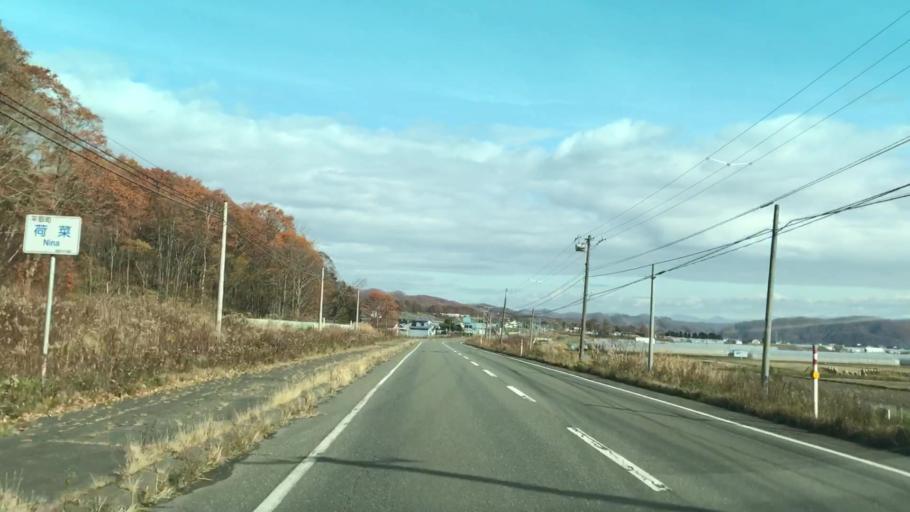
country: JP
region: Hokkaido
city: Shizunai-furukawacho
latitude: 42.5684
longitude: 142.0956
